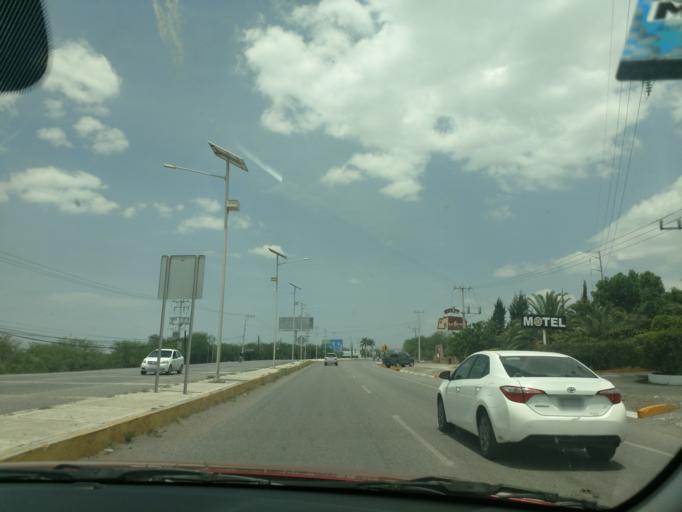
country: MX
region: San Luis Potosi
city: Rio Verde
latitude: 21.9216
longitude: -99.9633
